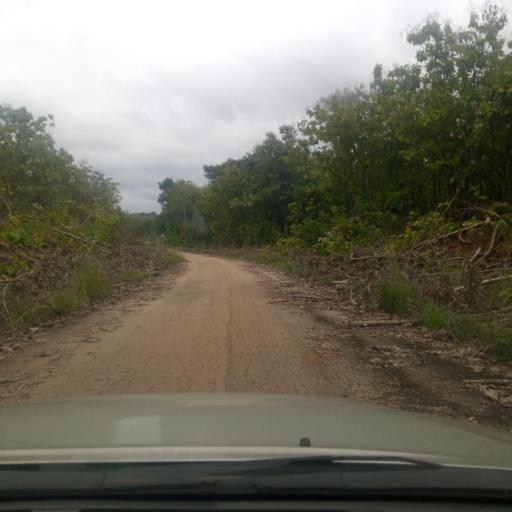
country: NG
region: Ebonyi
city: Effium
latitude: 6.6187
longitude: 8.0434
